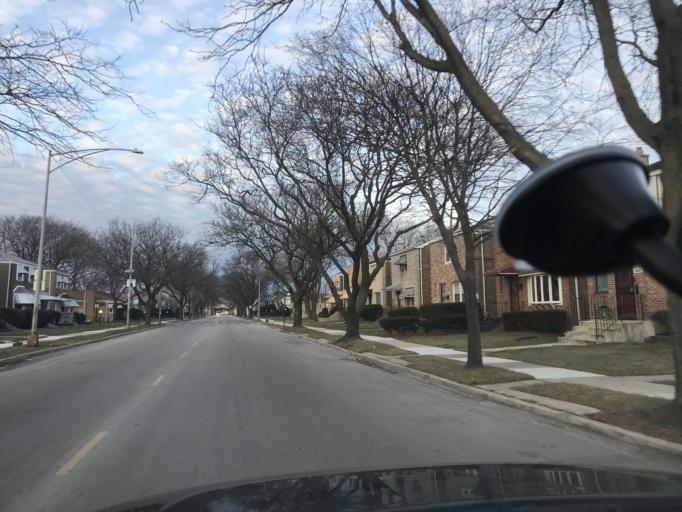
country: US
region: Indiana
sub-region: Lake County
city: Whiting
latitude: 41.7381
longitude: -87.5757
